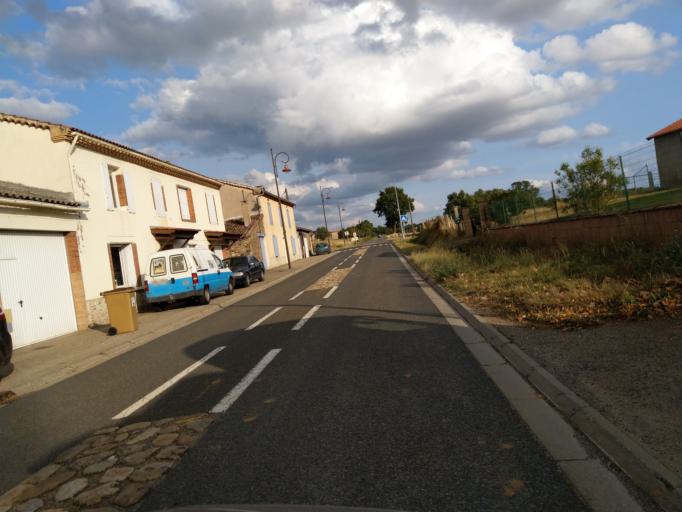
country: FR
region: Midi-Pyrenees
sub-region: Departement du Tarn
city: Frejairolles
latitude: 43.8796
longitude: 2.2321
